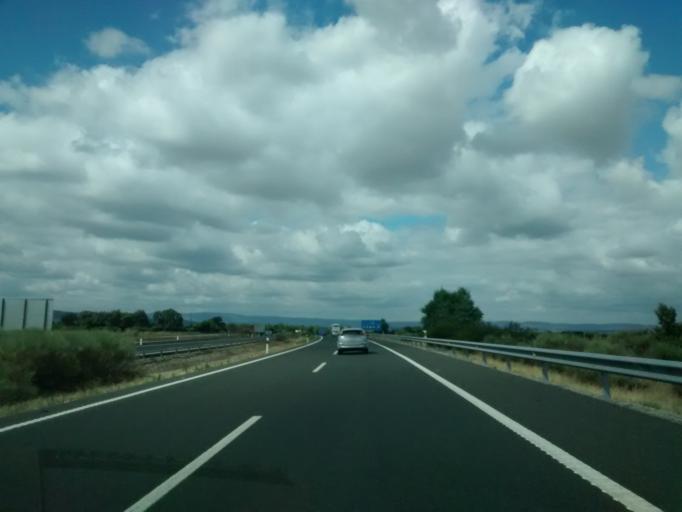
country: ES
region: Extremadura
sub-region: Provincia de Caceres
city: Millanes
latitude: 39.8619
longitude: -5.6095
